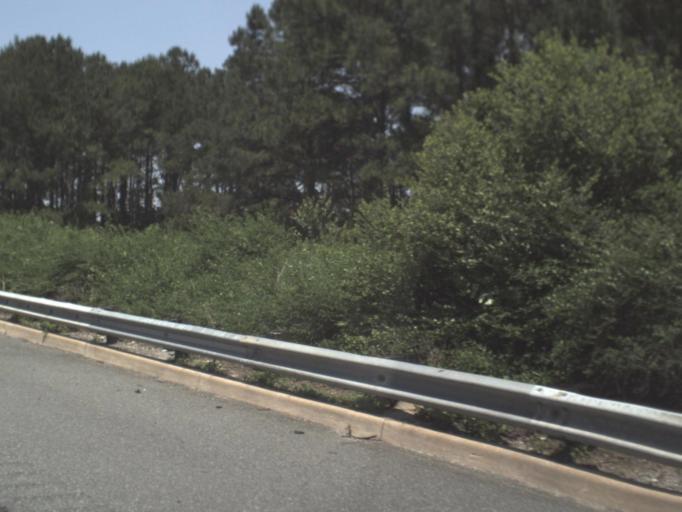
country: US
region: Florida
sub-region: Baker County
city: Macclenny
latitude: 30.2617
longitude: -82.1617
